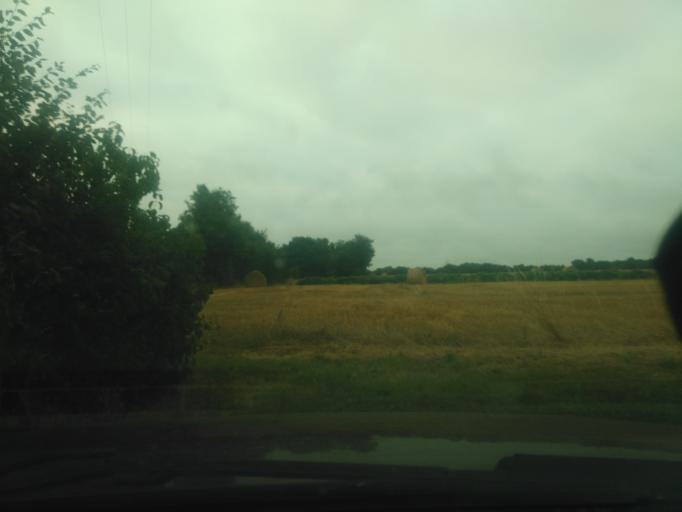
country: FR
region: Pays de la Loire
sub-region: Departement de la Vendee
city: Saint-Denis-la-Chevasse
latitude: 46.7934
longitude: -1.3172
